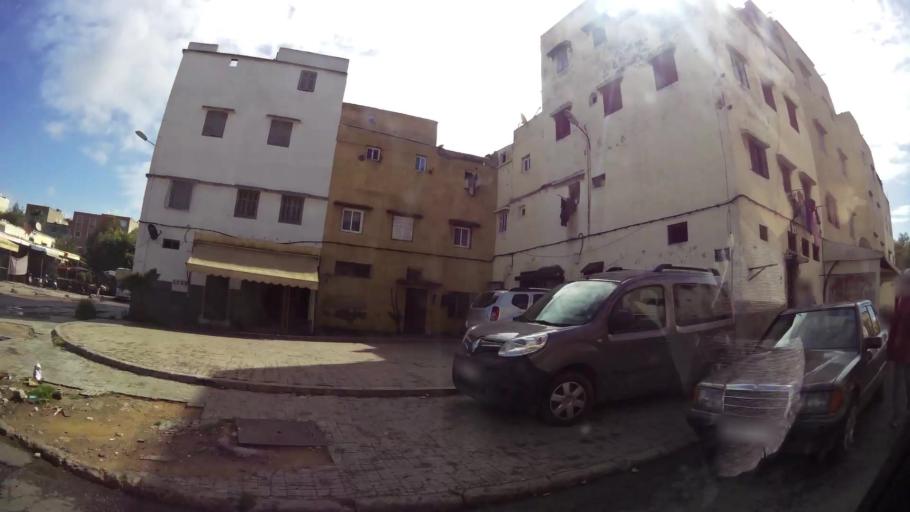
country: MA
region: Grand Casablanca
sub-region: Casablanca
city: Casablanca
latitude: 33.5697
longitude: -7.6759
